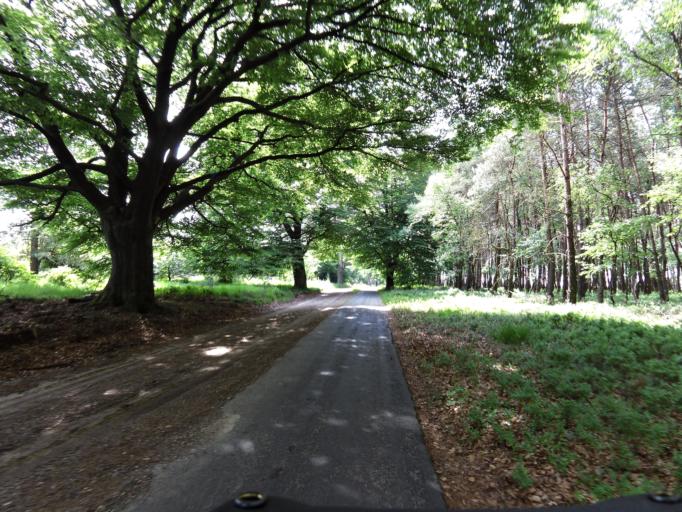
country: NL
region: Gelderland
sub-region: Gemeente Rozendaal
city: Rozendaal
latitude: 52.0488
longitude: 5.9811
